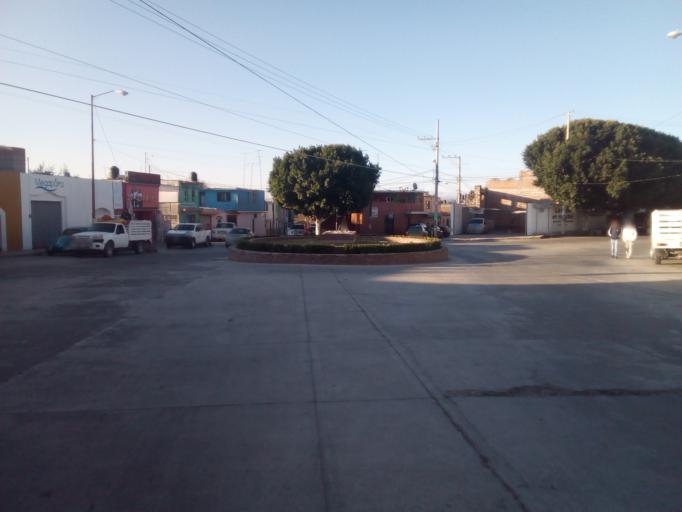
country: MX
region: Guerrero
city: San Luis de la Paz
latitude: 21.2932
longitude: -100.5149
